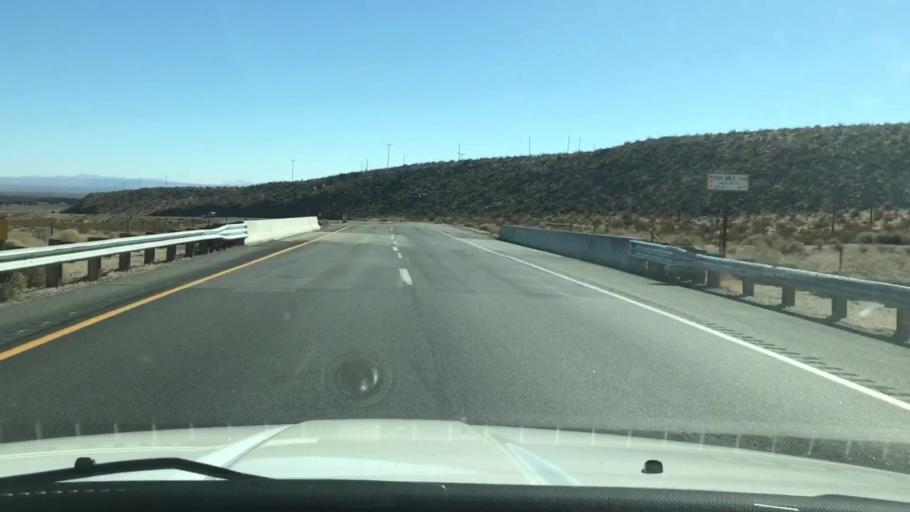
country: US
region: California
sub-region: Kern County
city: Inyokern
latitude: 35.8739
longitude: -117.8883
